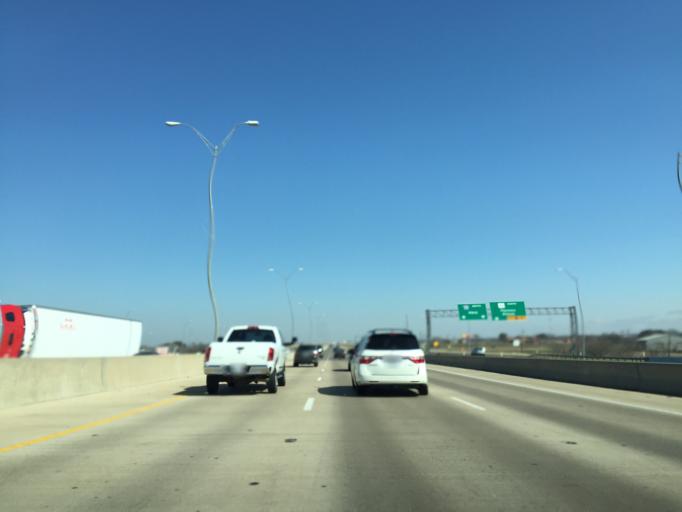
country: US
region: Texas
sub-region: Williamson County
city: Serenada
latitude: 30.6915
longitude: -97.6558
